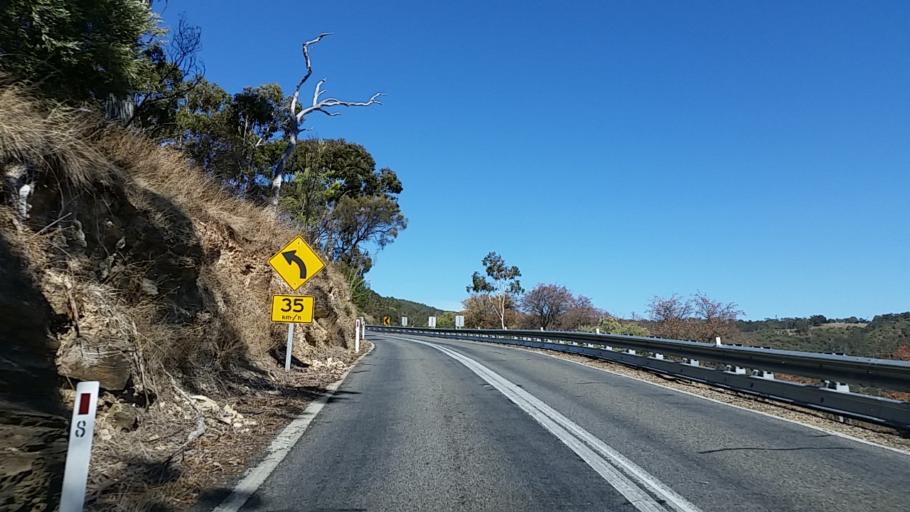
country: AU
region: South Australia
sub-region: Burnside
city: Beaumont
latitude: -34.9485
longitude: 138.6720
